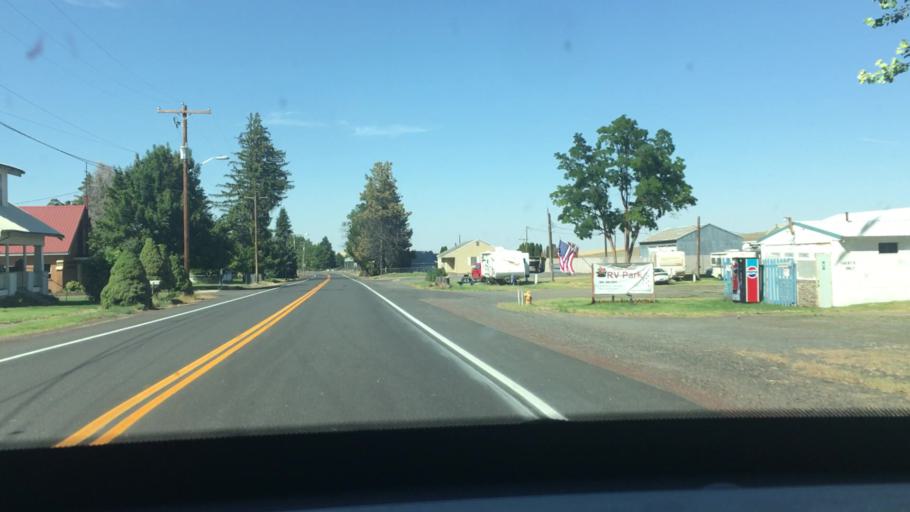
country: US
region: Oregon
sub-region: Sherman County
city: Moro
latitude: 45.3631
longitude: -120.7831
